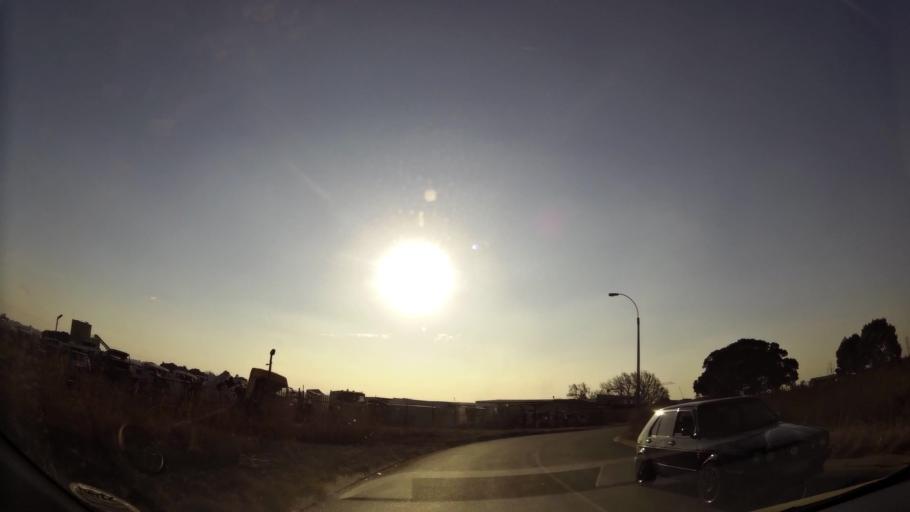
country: ZA
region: Gauteng
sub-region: West Rand District Municipality
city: Randfontein
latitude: -26.2033
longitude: 27.6887
